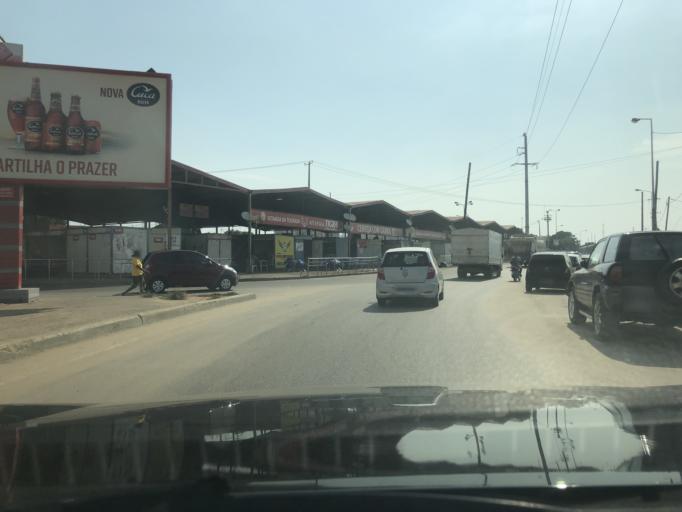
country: AO
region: Luanda
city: Luanda
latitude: -8.8395
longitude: 13.2522
